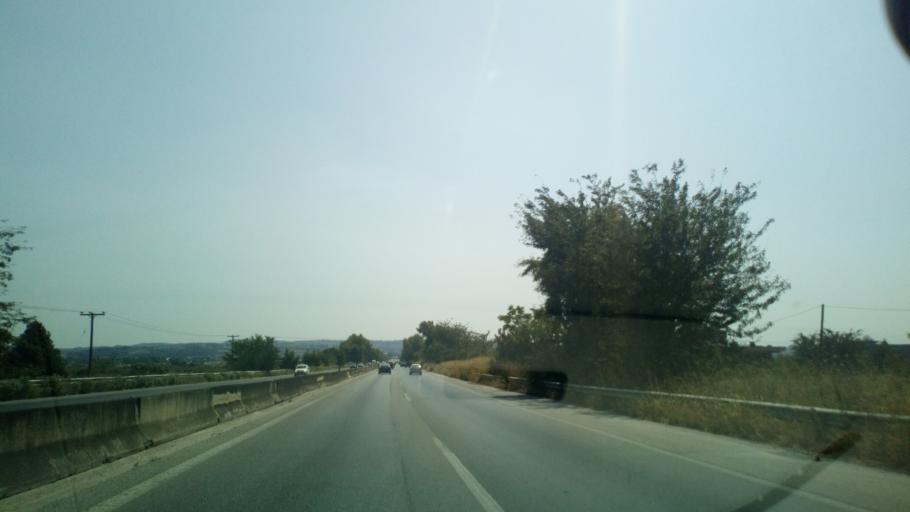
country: GR
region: Central Macedonia
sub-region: Nomos Thessalonikis
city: Thermi
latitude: 40.5242
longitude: 23.0124
